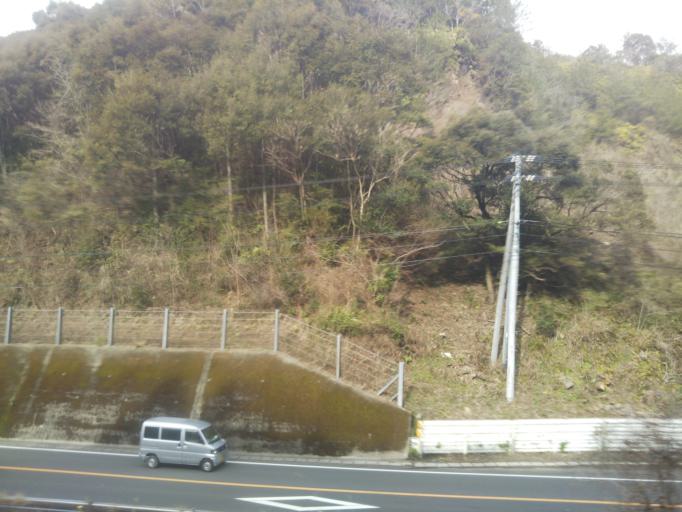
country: JP
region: Kochi
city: Nakamura
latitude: 32.9978
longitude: 132.9669
